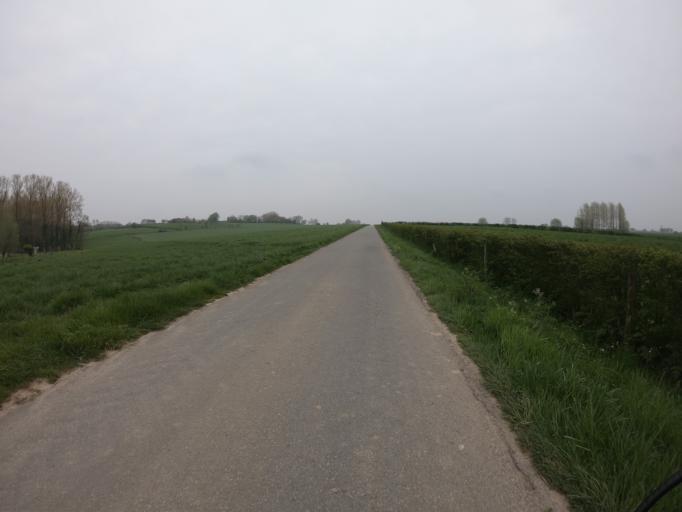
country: BE
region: Wallonia
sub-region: Province du Hainaut
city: Flobecq
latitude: 50.7535
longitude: 3.7740
